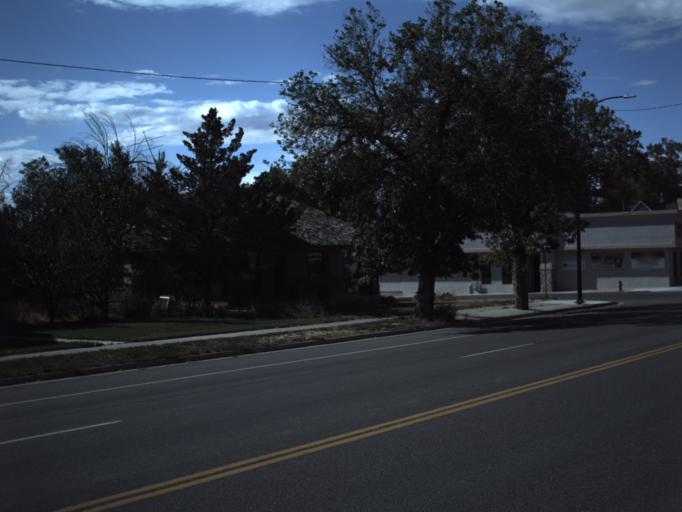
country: US
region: Utah
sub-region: Sanpete County
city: Ephraim
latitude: 39.3575
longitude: -111.5871
